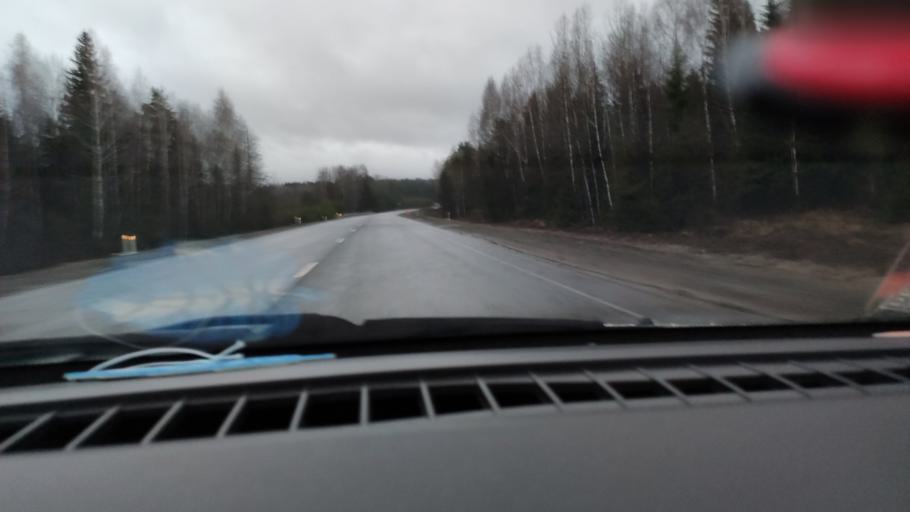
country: RU
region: Udmurtiya
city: Alnashi
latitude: 56.1030
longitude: 52.4582
